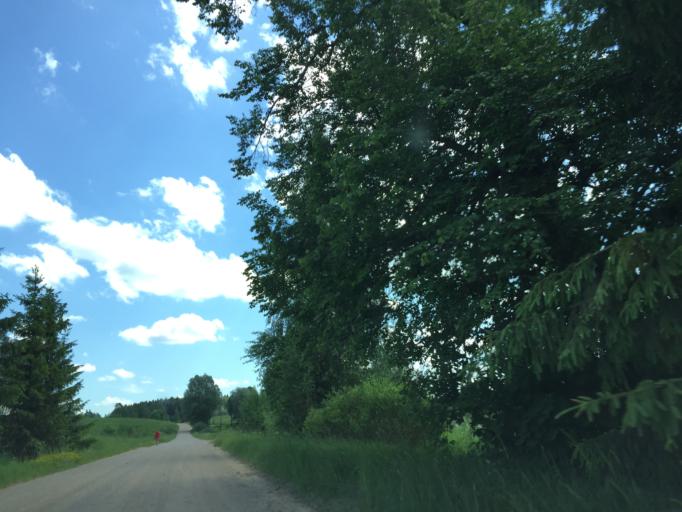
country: LV
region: Priekuli
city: Priekuli
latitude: 57.2566
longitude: 25.4284
